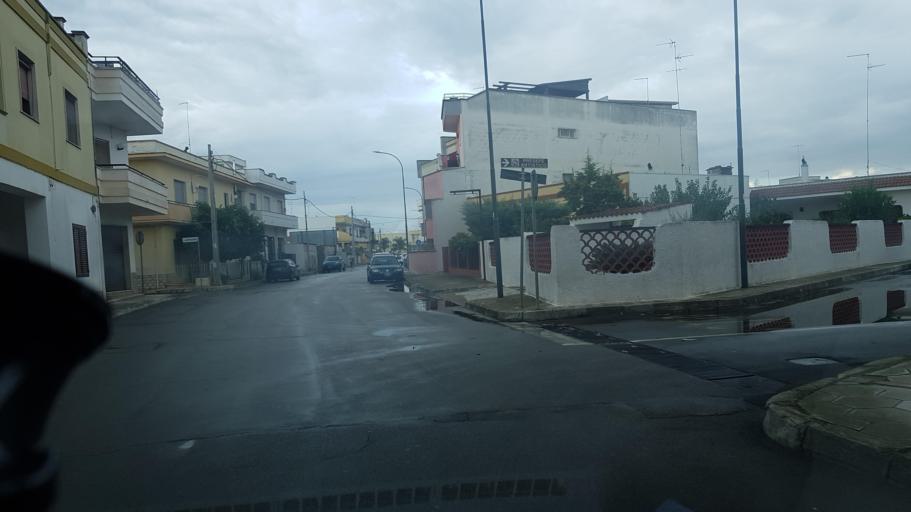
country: IT
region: Apulia
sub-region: Provincia di Lecce
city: Salice Salentino
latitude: 40.3884
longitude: 17.9596
